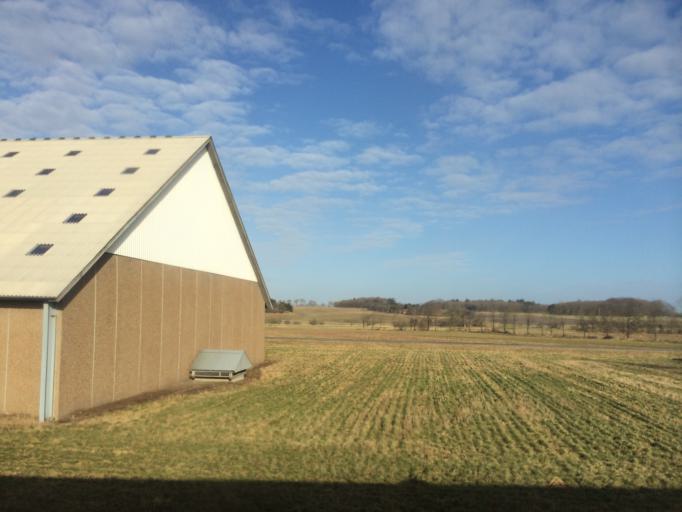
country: DK
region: Central Jutland
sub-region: Herning Kommune
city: Snejbjerg
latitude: 56.1648
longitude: 8.8827
